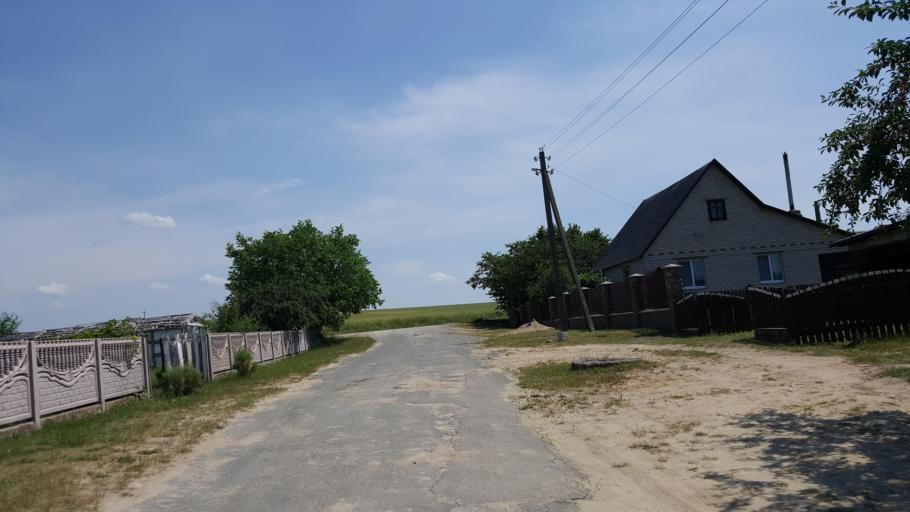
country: BY
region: Brest
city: Kamyanyets
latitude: 52.4099
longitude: 23.8348
